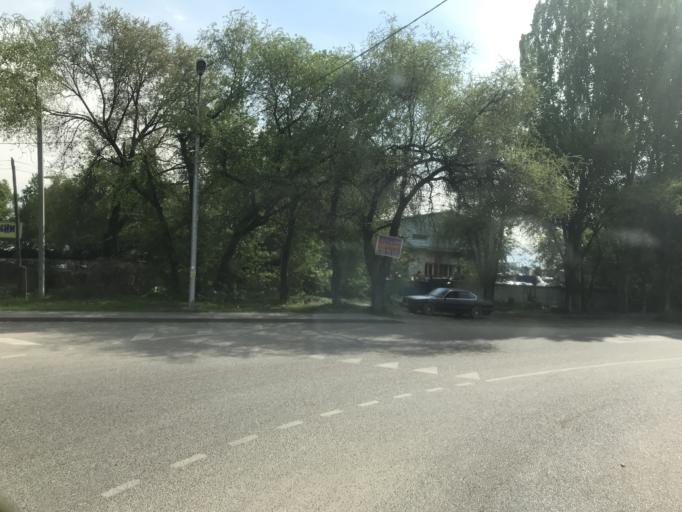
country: KZ
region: Almaty Qalasy
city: Almaty
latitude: 43.2399
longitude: 76.8059
